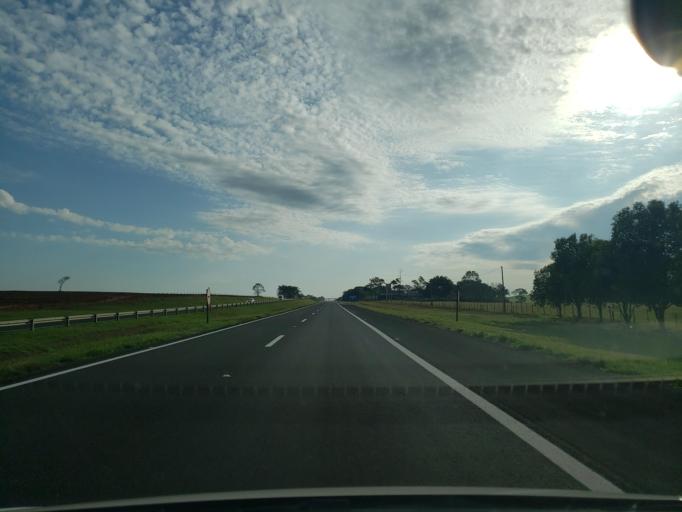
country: BR
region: Sao Paulo
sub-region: Valparaiso
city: Valparaiso
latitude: -21.2061
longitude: -50.7736
